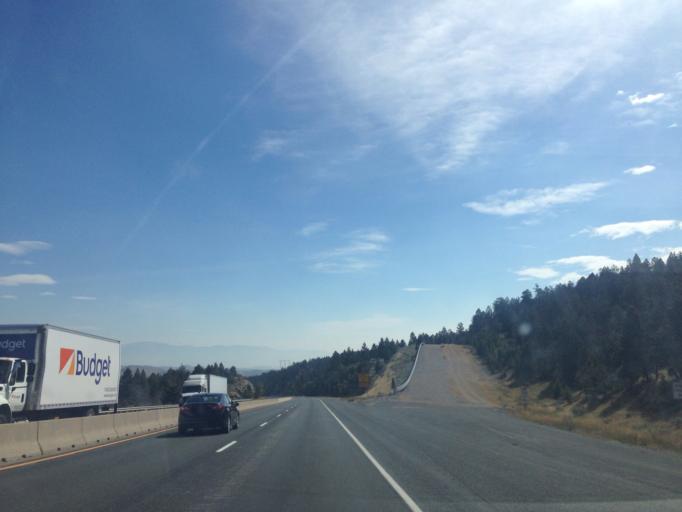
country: US
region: Montana
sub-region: Jefferson County
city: Whitehall
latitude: 45.9101
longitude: -112.3124
